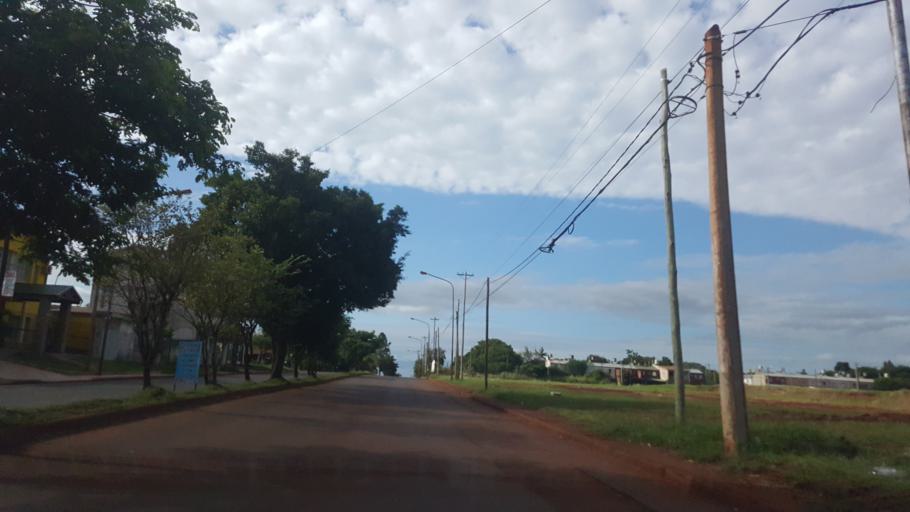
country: AR
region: Misiones
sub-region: Departamento de Capital
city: Posadas
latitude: -27.3872
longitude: -55.9345
